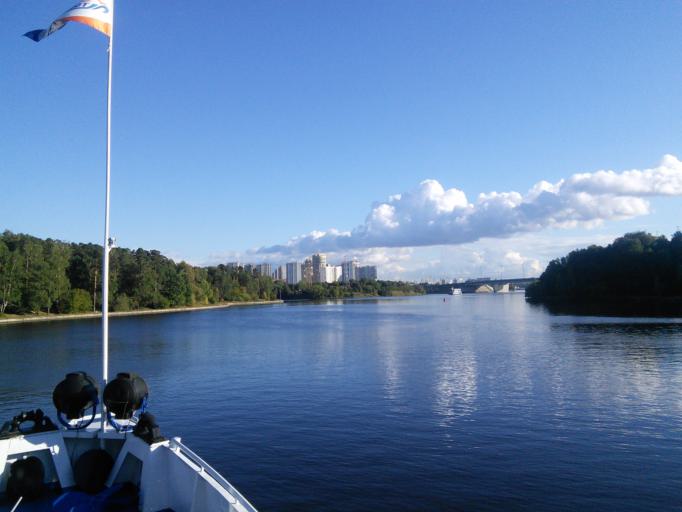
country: RU
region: Moskovskaya
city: Levoberezhnaya
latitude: 55.8816
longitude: 37.4576
